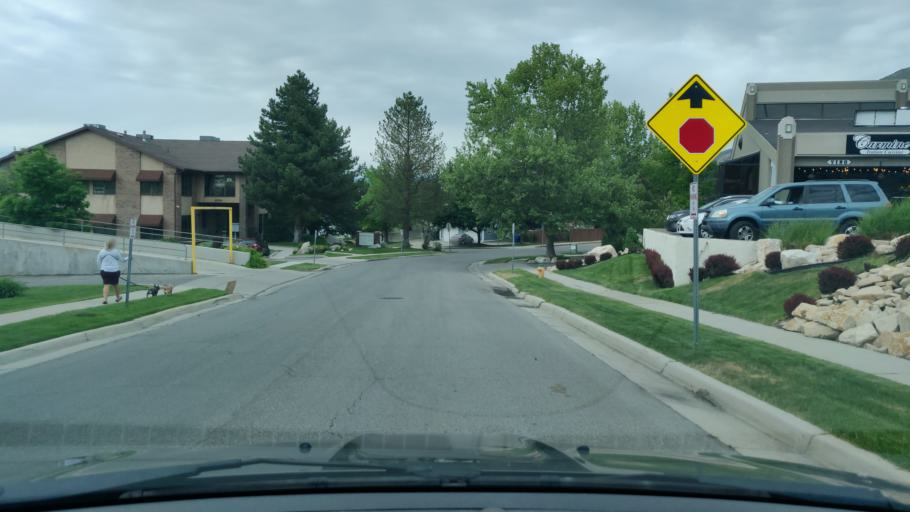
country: US
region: Utah
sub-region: Salt Lake County
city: Cottonwood Heights
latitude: 40.6246
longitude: -111.8205
